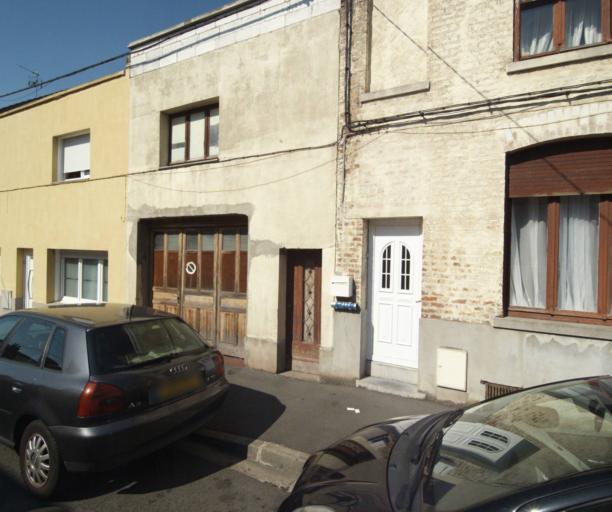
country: FR
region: Nord-Pas-de-Calais
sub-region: Departement du Nord
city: Mons-en-Baroeul
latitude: 50.6346
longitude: 3.1133
